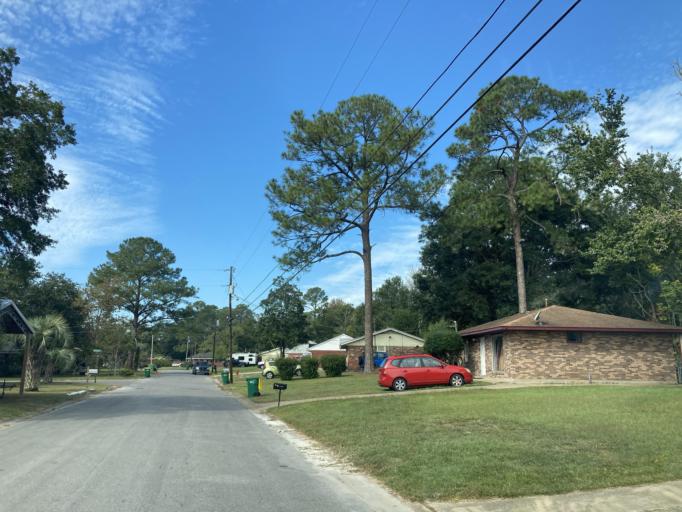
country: US
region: Mississippi
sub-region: Jackson County
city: Saint Martin
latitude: 30.4478
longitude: -88.8709
